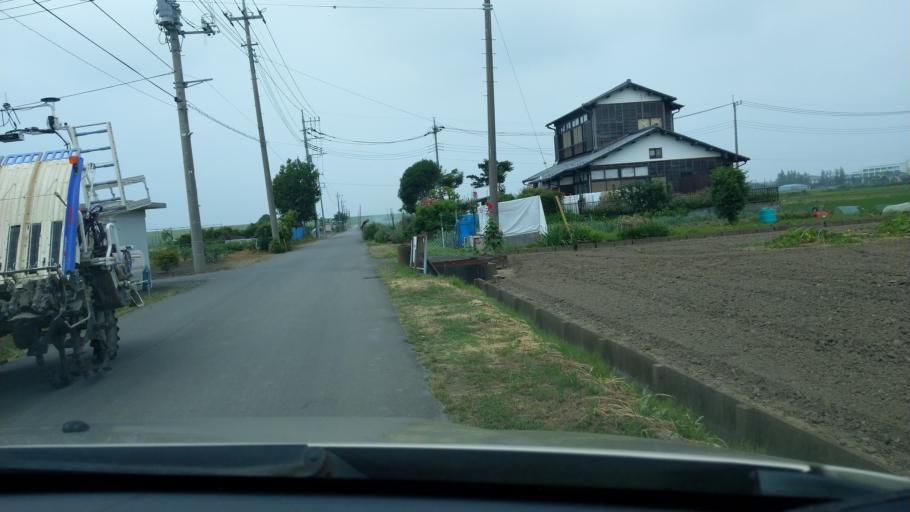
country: JP
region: Saitama
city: Yono
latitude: 35.8825
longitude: 139.5908
